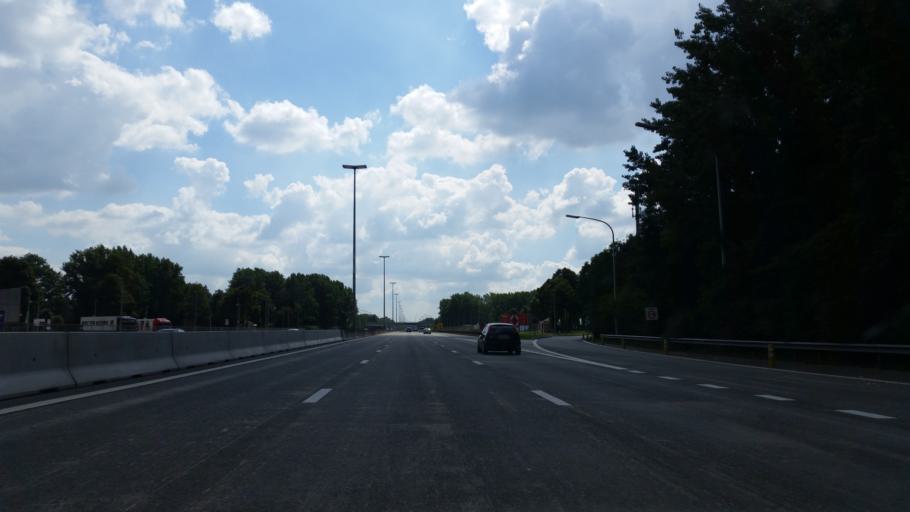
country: BE
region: Flanders
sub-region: Provincie Oost-Vlaanderen
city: Zulte
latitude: 50.8986
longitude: 3.4780
